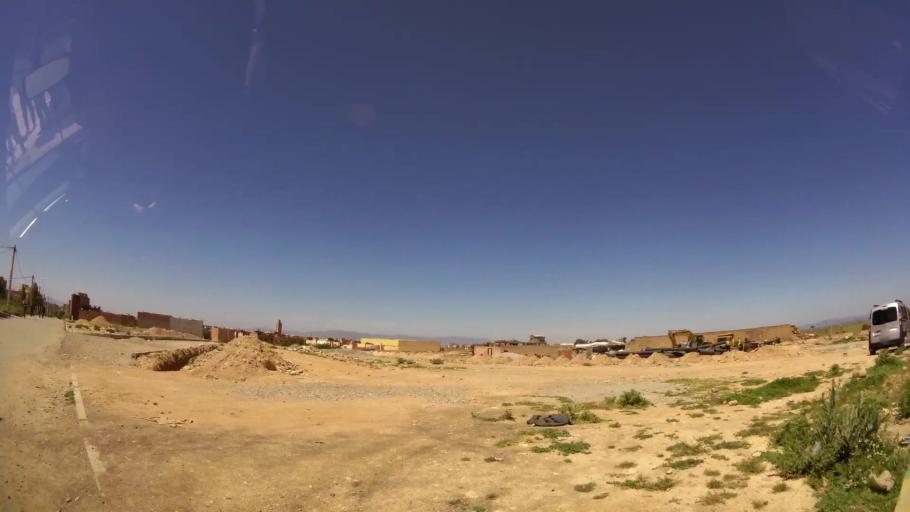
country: MA
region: Oriental
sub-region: Oujda-Angad
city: Oujda
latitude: 34.6606
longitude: -1.8686
